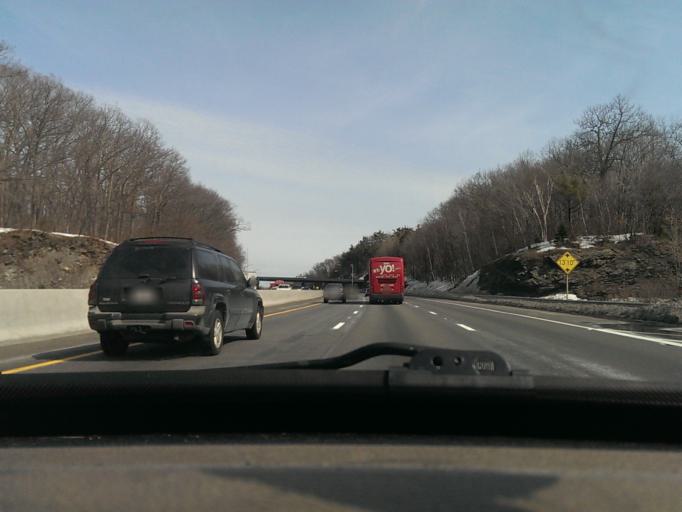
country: US
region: Massachusetts
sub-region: Worcester County
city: Auburn
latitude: 42.1916
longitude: -71.8573
